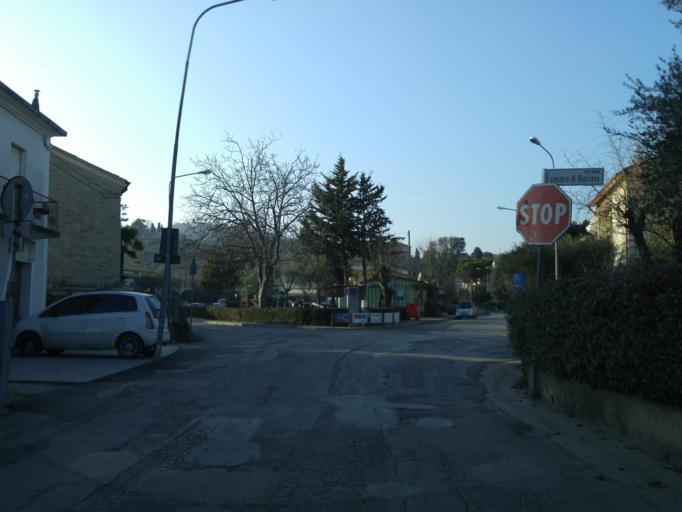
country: IT
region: The Marches
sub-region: Provincia di Pesaro e Urbino
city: Rosciano
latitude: 43.8183
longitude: 12.9942
